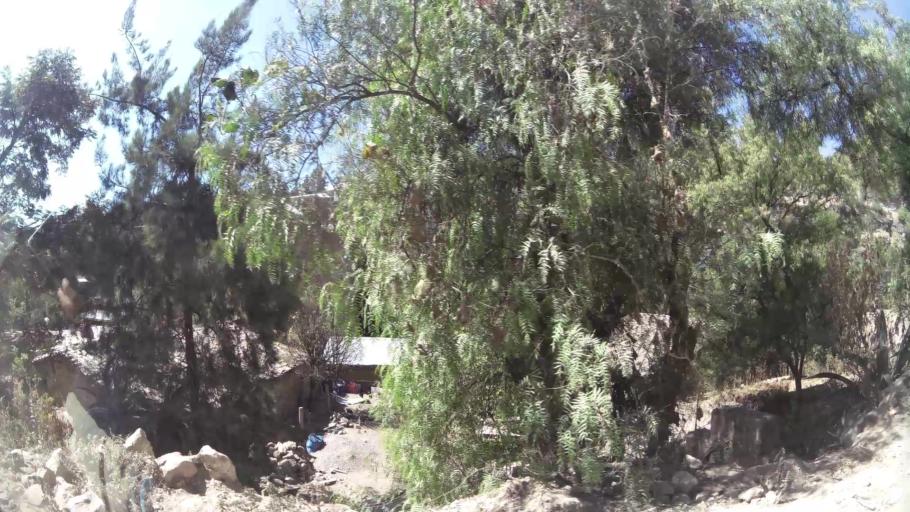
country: PE
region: Ayacucho
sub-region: Provincia de Huamanga
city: Carmen Alto
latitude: -13.1770
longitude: -74.2286
